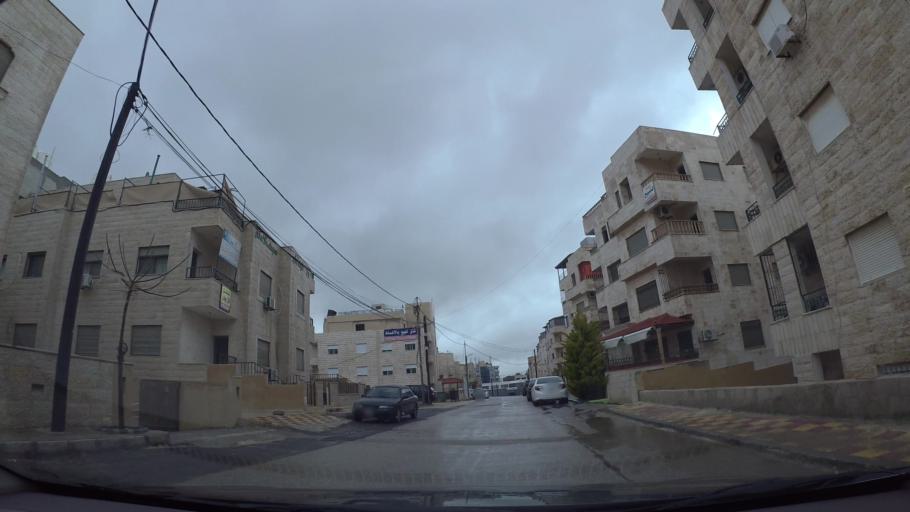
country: JO
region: Amman
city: Al Jubayhah
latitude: 32.0266
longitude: 35.8698
